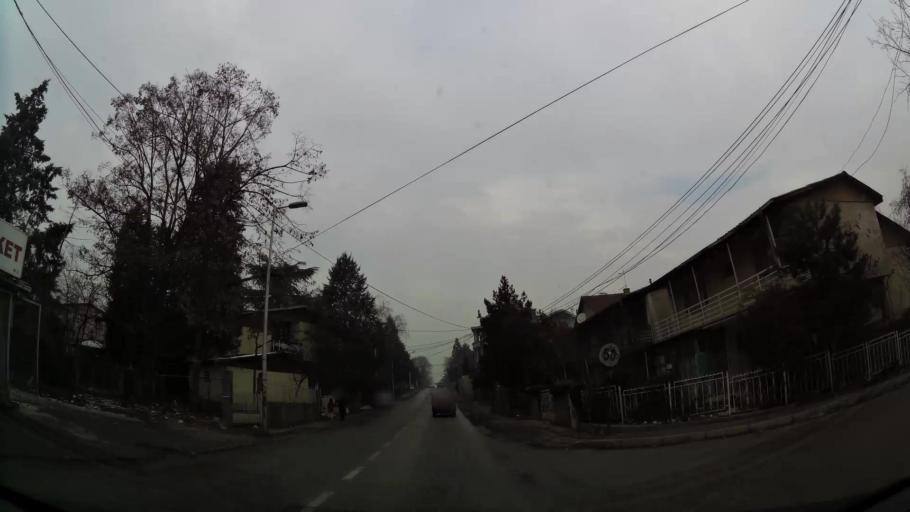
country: MK
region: Cair
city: Cair
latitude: 42.0177
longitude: 21.4531
